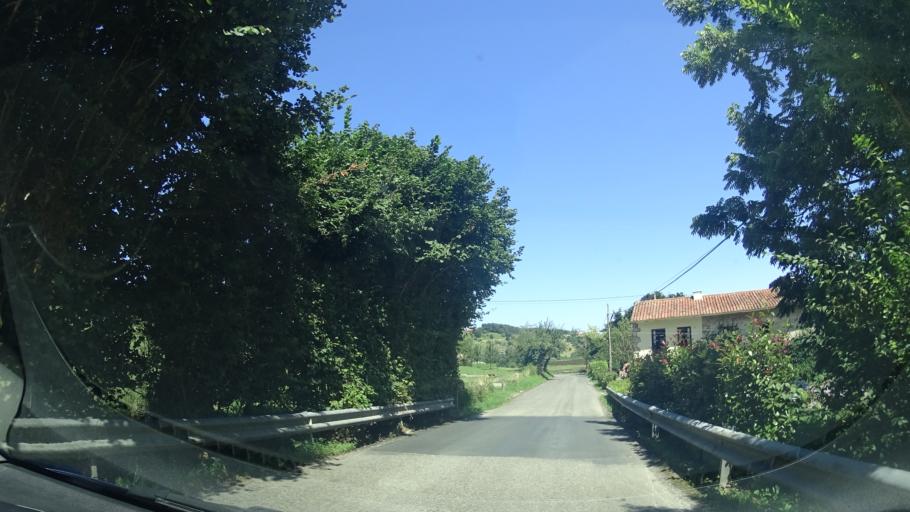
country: ES
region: Asturias
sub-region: Province of Asturias
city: Ribadesella
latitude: 43.4488
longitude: -5.0721
